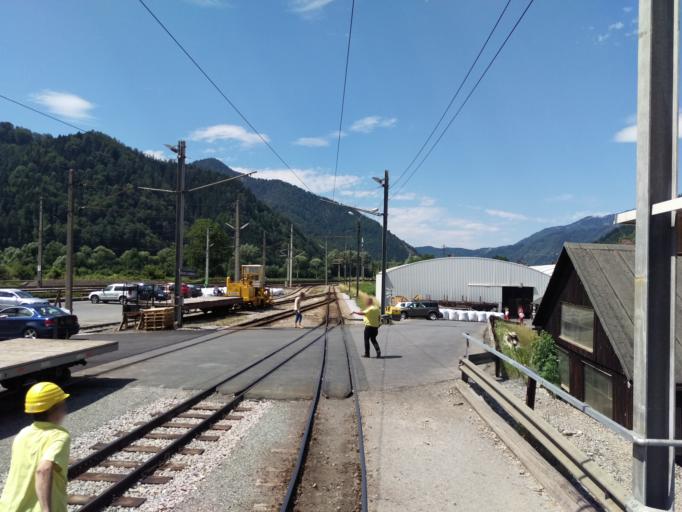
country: AT
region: Styria
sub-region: Politischer Bezirk Graz-Umgebung
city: Rothelstein
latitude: 47.3337
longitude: 15.3589
